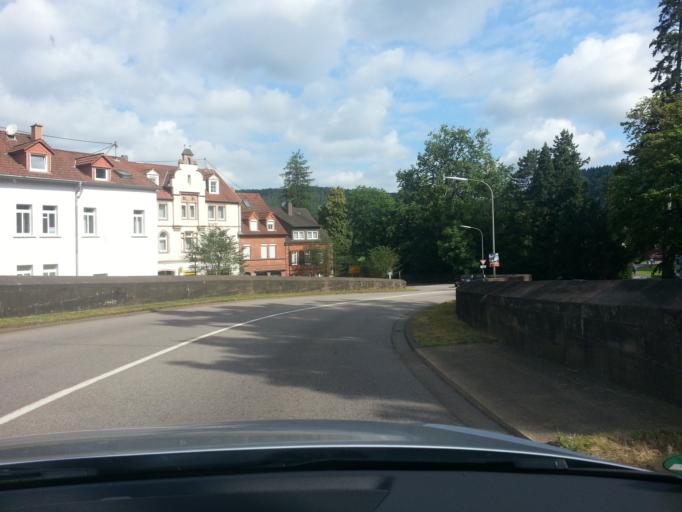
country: DE
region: Saarland
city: Mettlach
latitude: 49.4919
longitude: 6.5931
